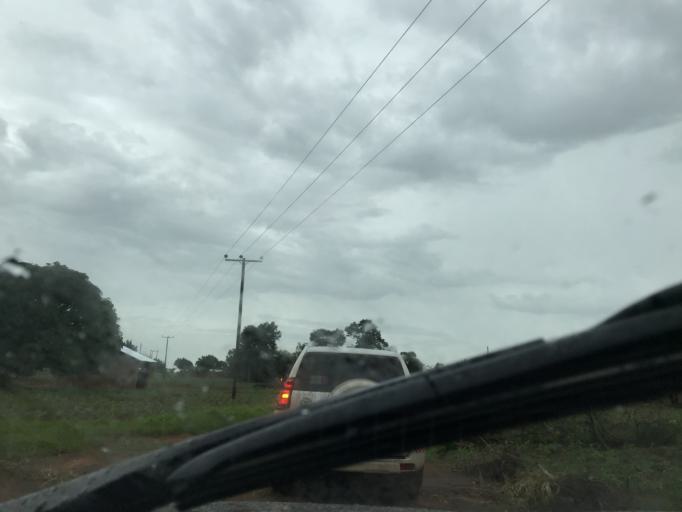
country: GH
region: Upper West
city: Wa
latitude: 10.5133
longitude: -2.7041
